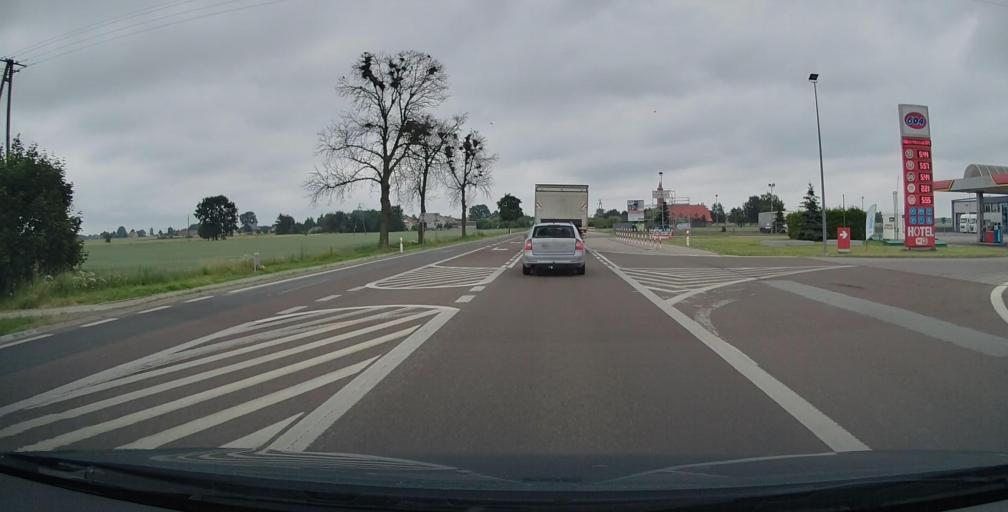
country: PL
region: Lublin Voivodeship
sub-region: Powiat bialski
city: Rzeczyca
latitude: 52.0239
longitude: 22.7175
